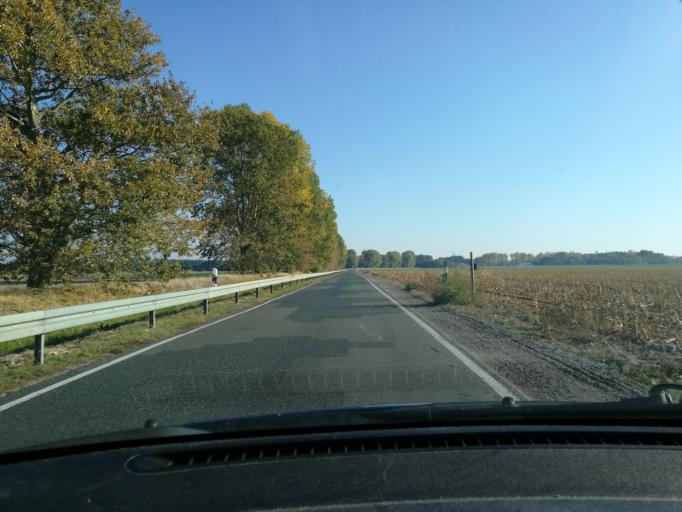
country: DE
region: Mecklenburg-Vorpommern
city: Domitz
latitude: 53.1549
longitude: 11.2487
